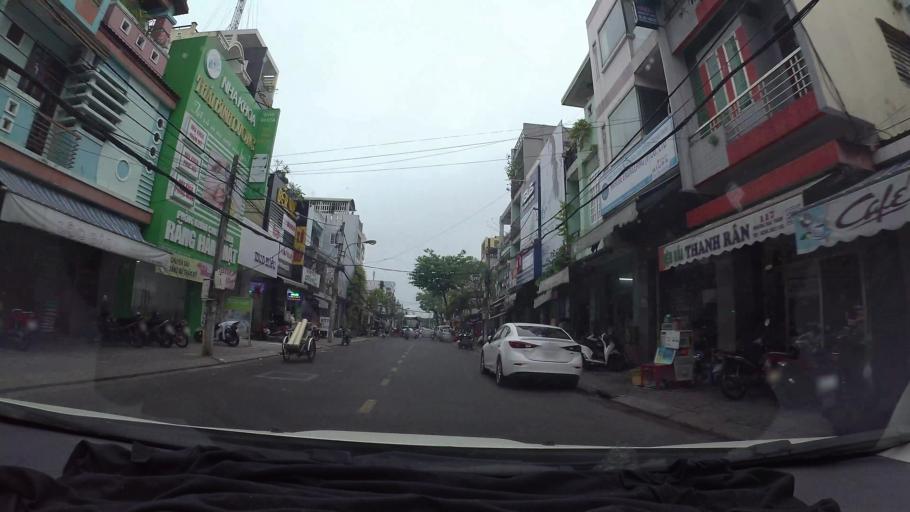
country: VN
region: Da Nang
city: Da Nang
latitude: 16.0674
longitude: 108.2102
